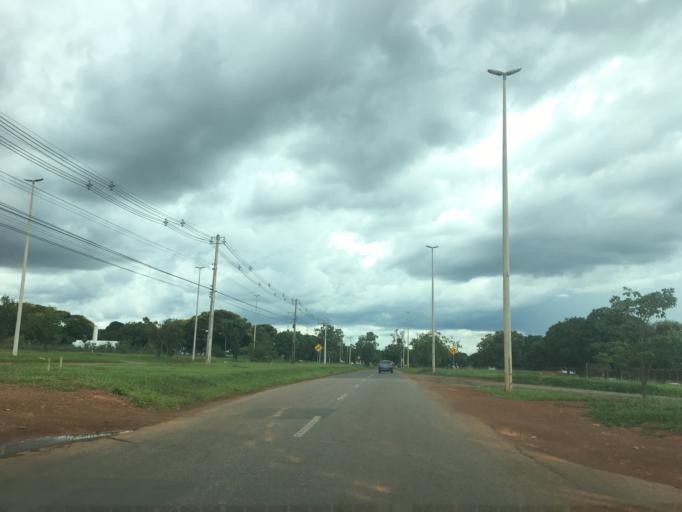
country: BR
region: Federal District
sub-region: Brasilia
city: Brasilia
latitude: -15.8325
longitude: -47.9411
